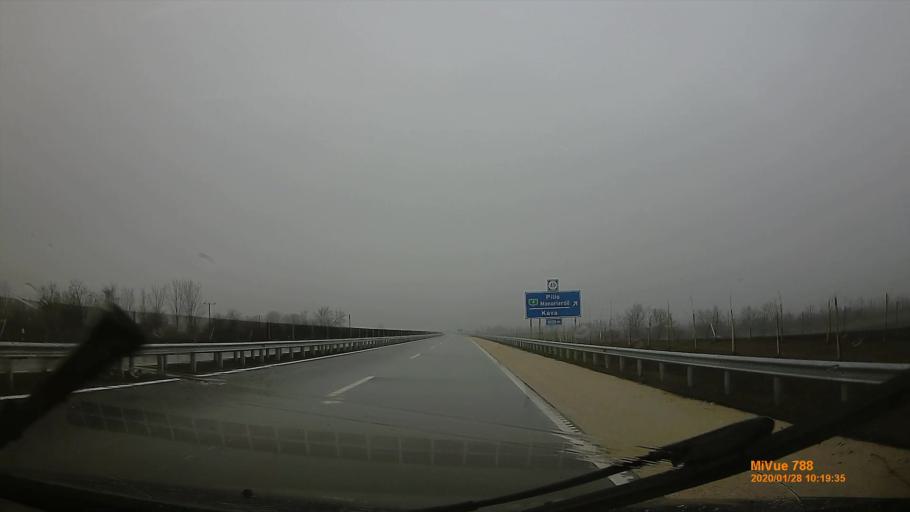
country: HU
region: Pest
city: Pilis
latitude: 47.3029
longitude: 19.5659
